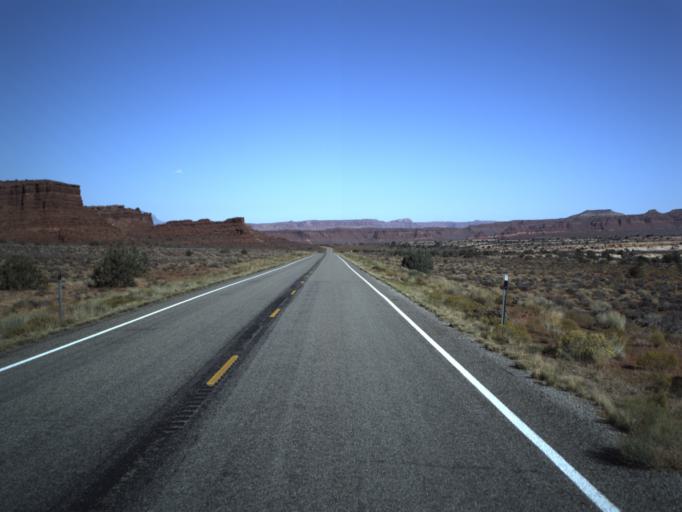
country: US
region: Utah
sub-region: San Juan County
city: Blanding
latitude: 37.7860
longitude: -110.2954
